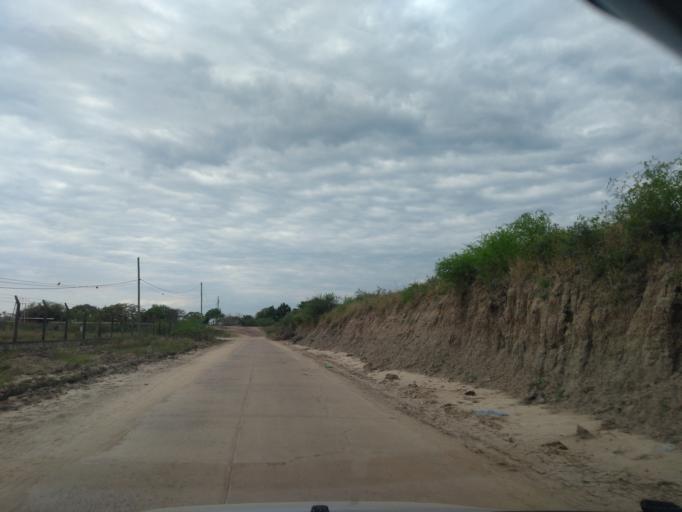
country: AR
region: Chaco
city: Puerto Vilelas
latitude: -27.5369
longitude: -58.9185
